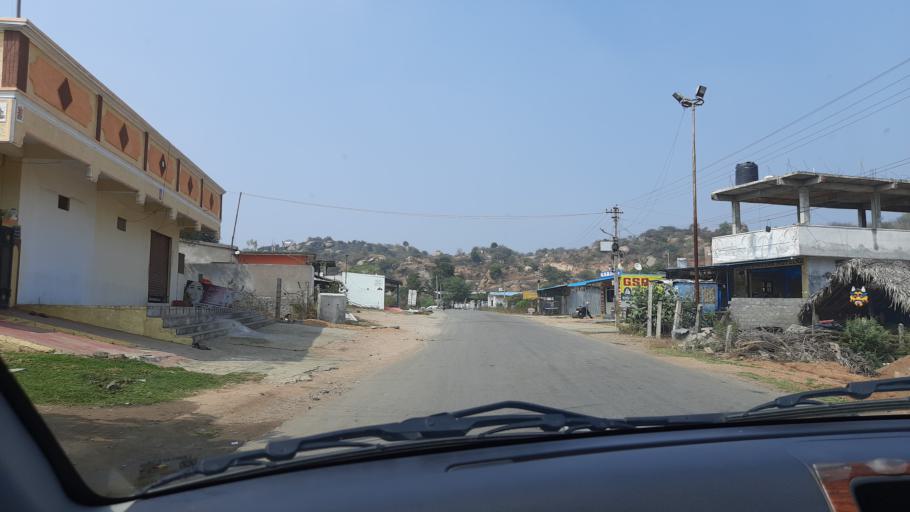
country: IN
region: Telangana
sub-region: Rangareddi
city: Lal Bahadur Nagar
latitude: 17.2741
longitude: 78.6677
